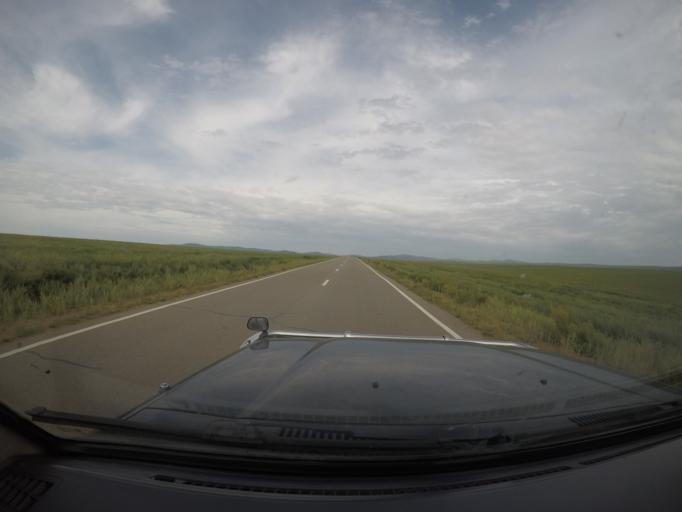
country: MN
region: Suhbaatar
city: Hanhohiy
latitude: 47.5728
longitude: 112.2339
